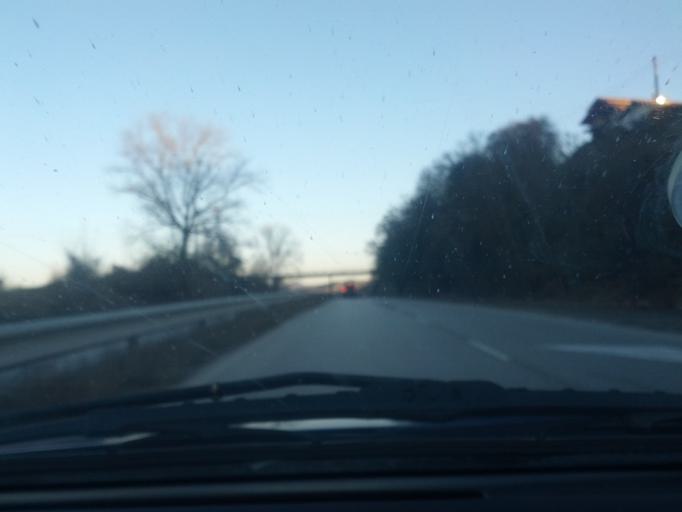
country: BG
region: Vratsa
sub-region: Obshtina Mezdra
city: Mezdra
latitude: 43.1410
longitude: 23.6939
